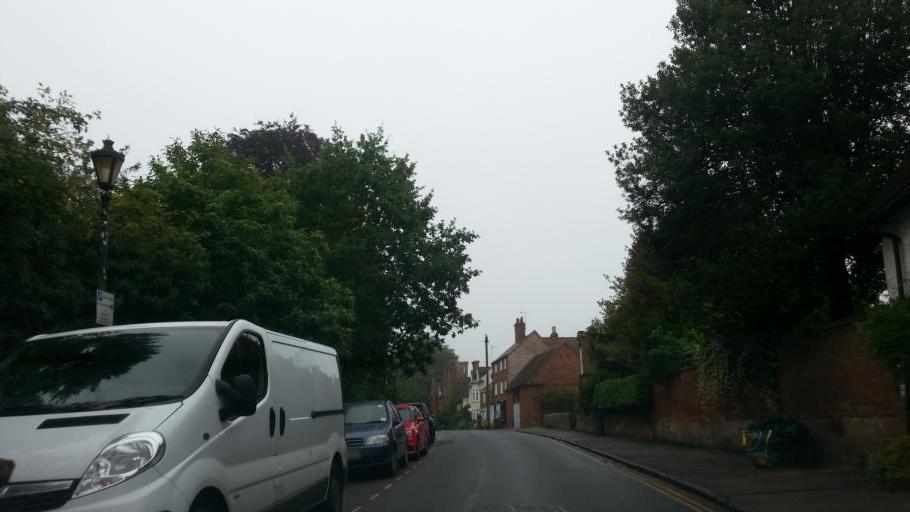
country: GB
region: England
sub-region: Warwickshire
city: Kenilworth
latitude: 52.3498
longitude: -1.5843
